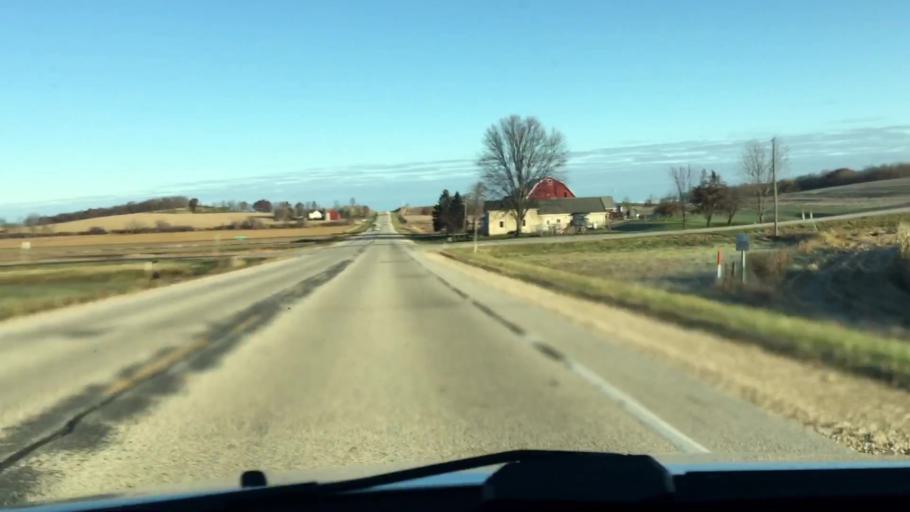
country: US
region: Wisconsin
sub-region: Dodge County
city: Theresa
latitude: 43.4706
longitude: -88.4501
